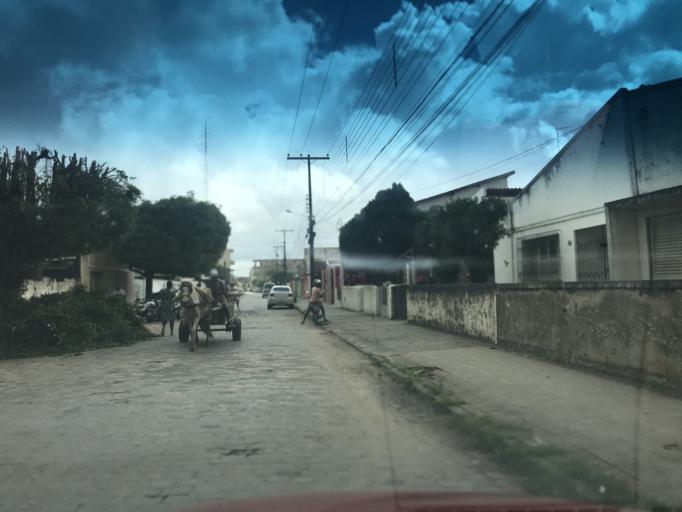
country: BR
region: Bahia
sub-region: Cruz Das Almas
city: Cruz das Almas
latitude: -12.6746
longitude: -39.0992
